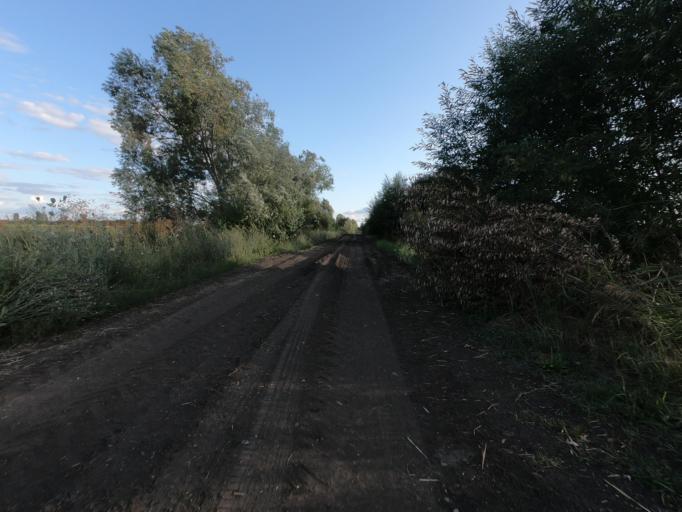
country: HU
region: Heves
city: Szihalom
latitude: 47.7225
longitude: 20.5514
